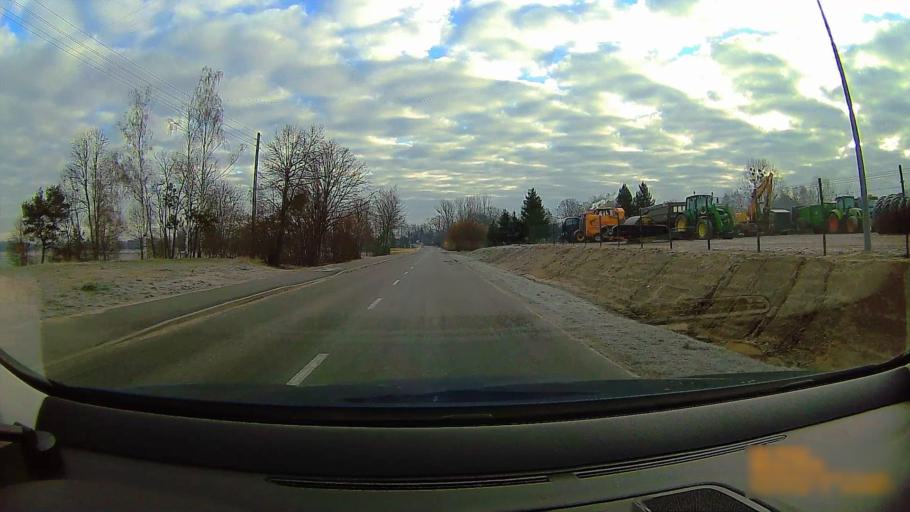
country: PL
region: Greater Poland Voivodeship
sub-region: Powiat koninski
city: Rzgow Pierwszy
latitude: 52.1676
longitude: 18.0808
